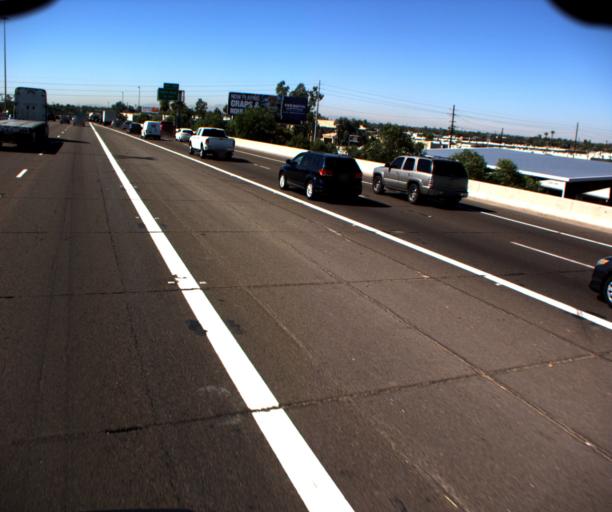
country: US
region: Arizona
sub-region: Maricopa County
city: Phoenix
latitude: 33.4621
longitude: -112.1153
